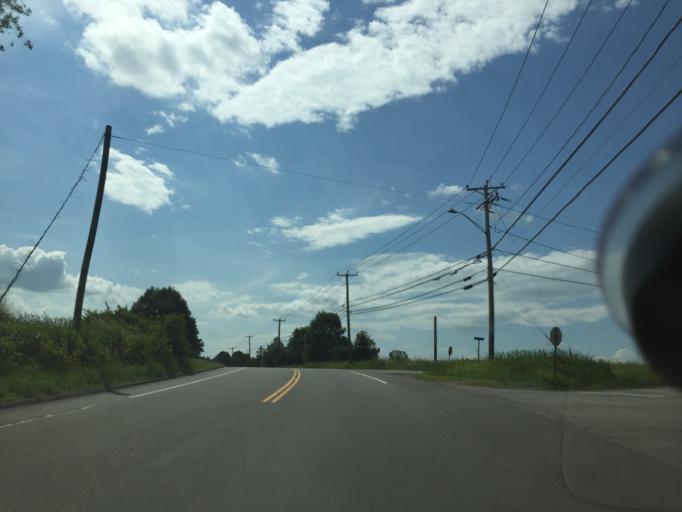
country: US
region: Connecticut
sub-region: Litchfield County
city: West Torrington
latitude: 41.8350
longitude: -73.1996
